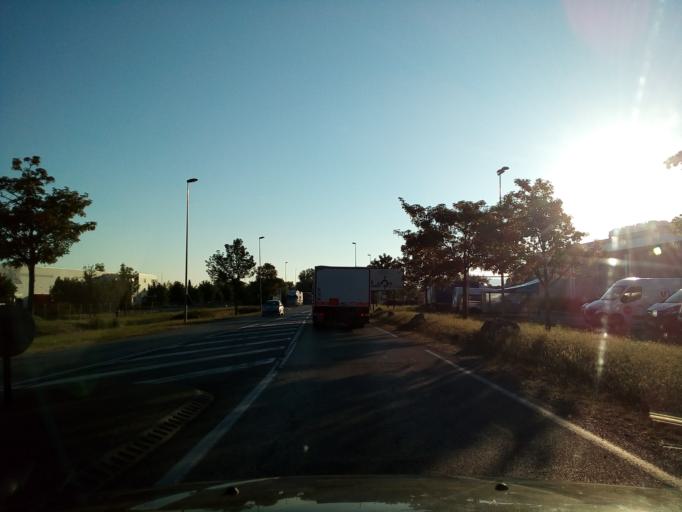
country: FR
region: Rhone-Alpes
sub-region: Departement de l'Isere
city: La Verpilliere
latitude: 45.6424
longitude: 5.1311
